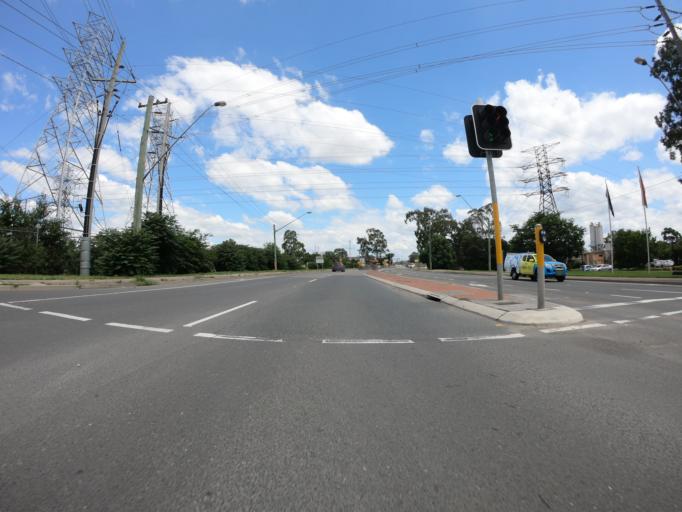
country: AU
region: New South Wales
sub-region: Penrith Municipality
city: Penrith
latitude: -33.7457
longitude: 150.6910
